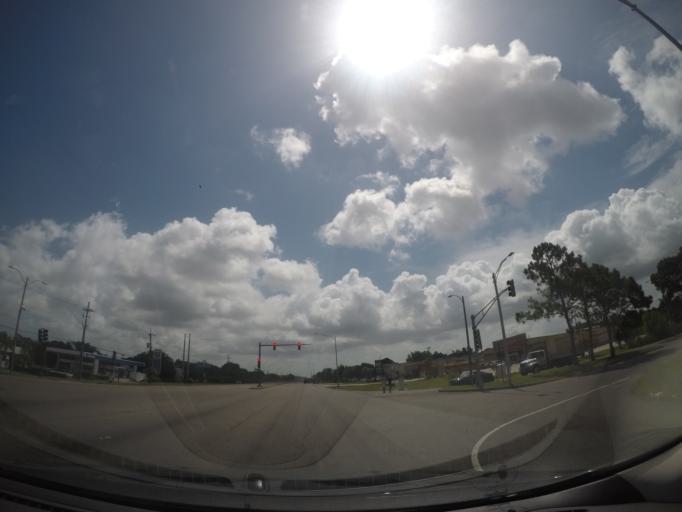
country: US
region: Louisiana
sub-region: Saint Bernard Parish
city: Chalmette
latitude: 30.0310
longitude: -89.9279
